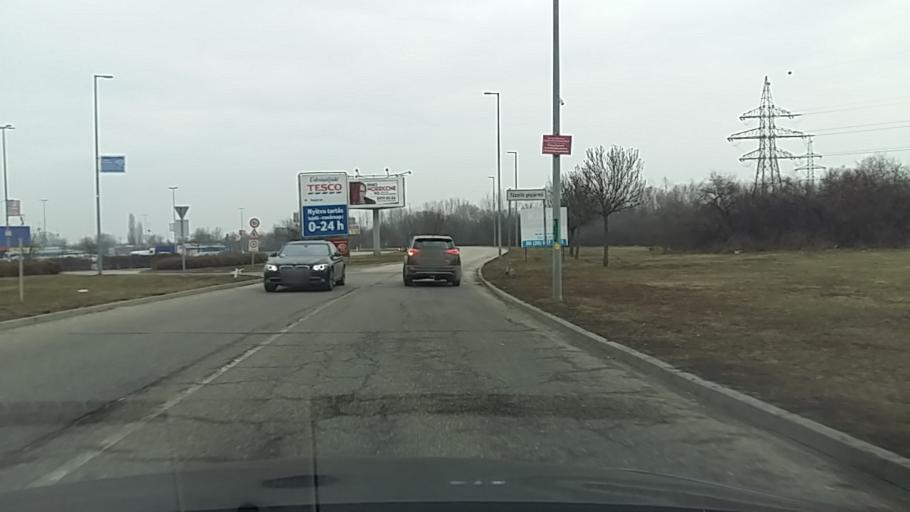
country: HU
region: Budapest
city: Budapest XIX. keruelet
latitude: 47.4260
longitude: 19.1485
